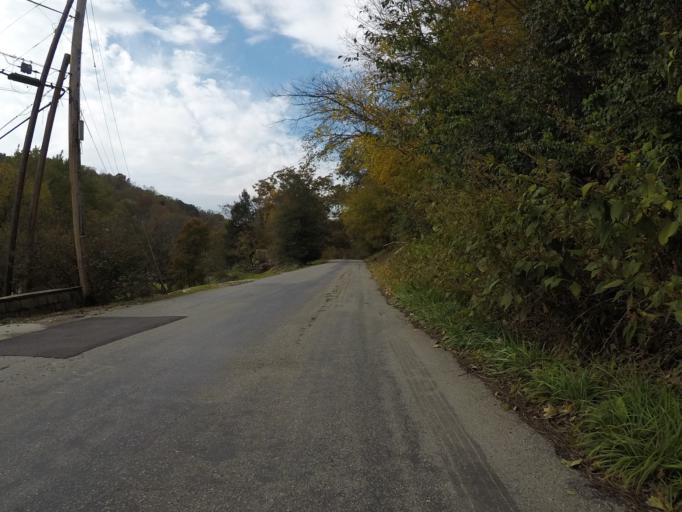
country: US
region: West Virginia
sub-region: Wayne County
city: Lavalette
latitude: 38.3363
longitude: -82.4453
